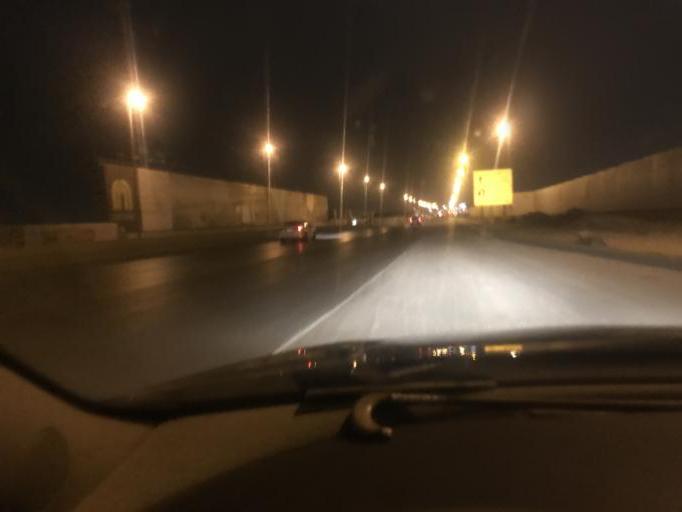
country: SA
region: Ar Riyad
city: Riyadh
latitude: 24.8106
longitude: 46.6709
